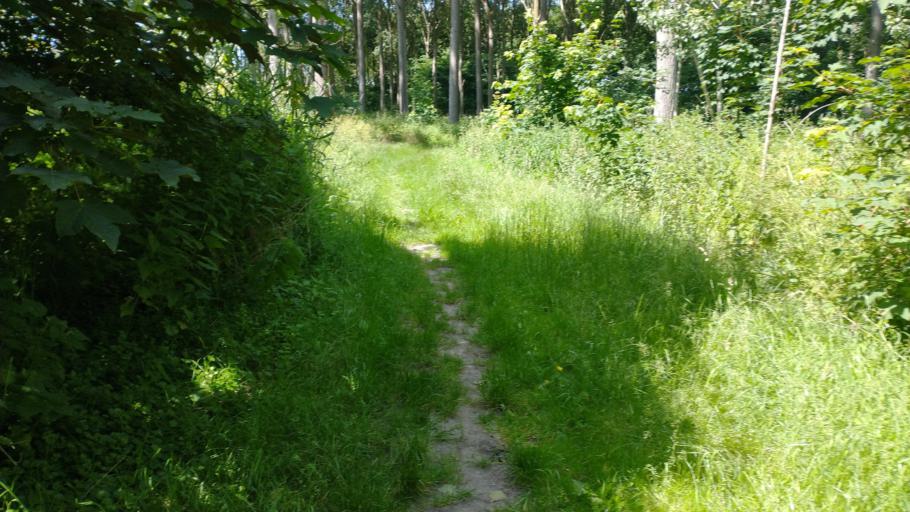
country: NL
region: North Holland
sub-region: Gemeente Huizen
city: Huizen
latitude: 52.3191
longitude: 5.2877
